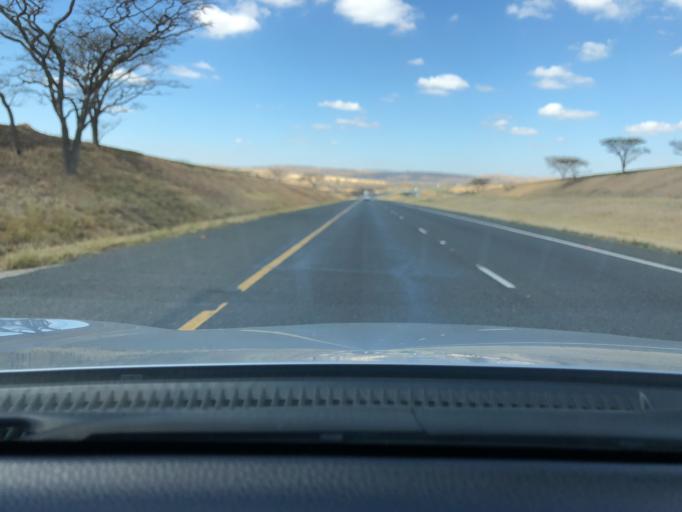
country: ZA
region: KwaZulu-Natal
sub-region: uThukela District Municipality
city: Estcourt
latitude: -28.9450
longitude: 29.7910
